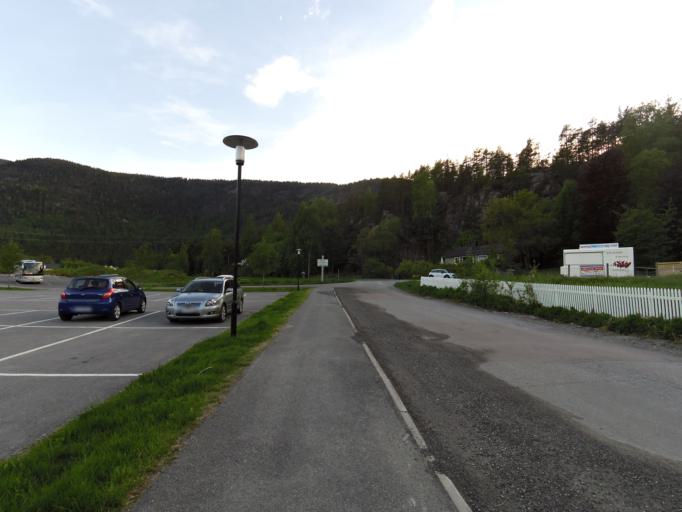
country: NO
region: Buskerud
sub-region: Fla
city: Fla
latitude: 60.4313
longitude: 9.4569
